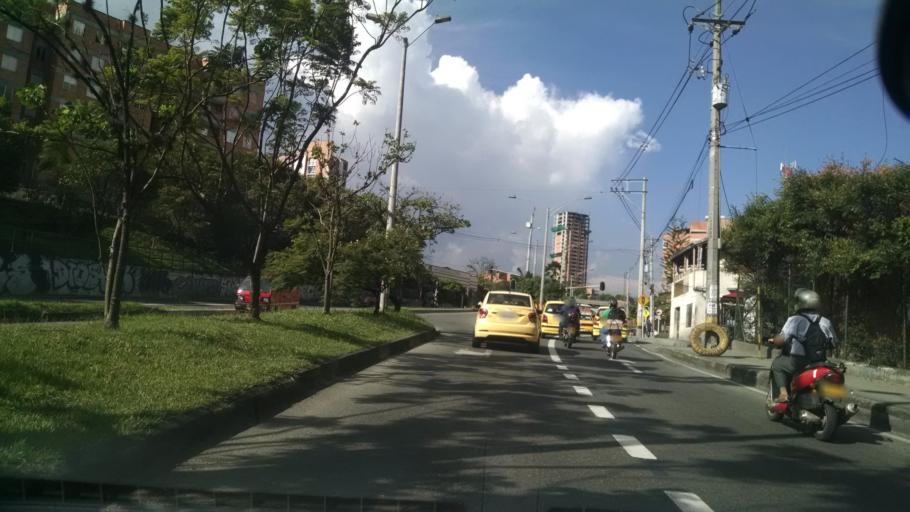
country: CO
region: Antioquia
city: Medellin
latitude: 6.2793
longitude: -75.5876
